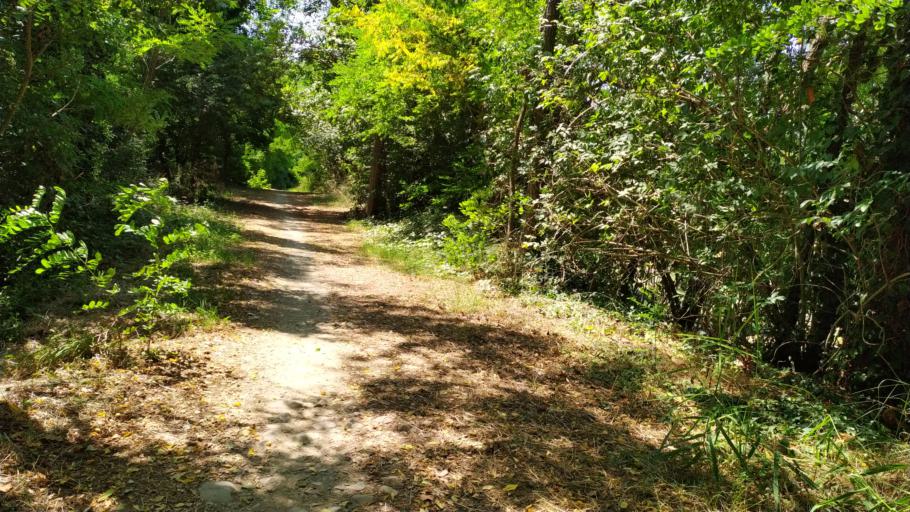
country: IT
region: Emilia-Romagna
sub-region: Forli-Cesena
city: Castrocaro Terme e Terra del Sole
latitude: 44.2035
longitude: 11.9981
